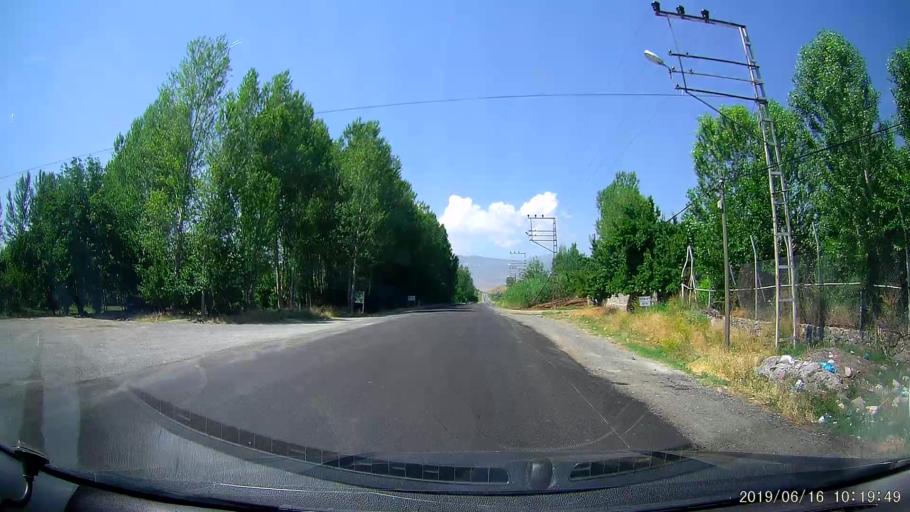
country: TR
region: Igdir
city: Tuzluca
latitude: 40.1526
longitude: 43.6531
